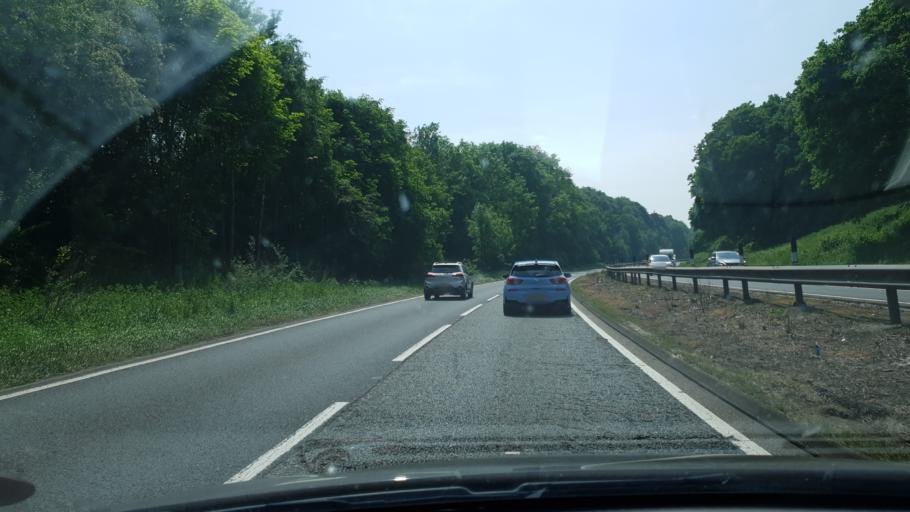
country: GB
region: England
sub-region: Suffolk
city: East Bergholt
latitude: 51.9598
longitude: 0.9715
